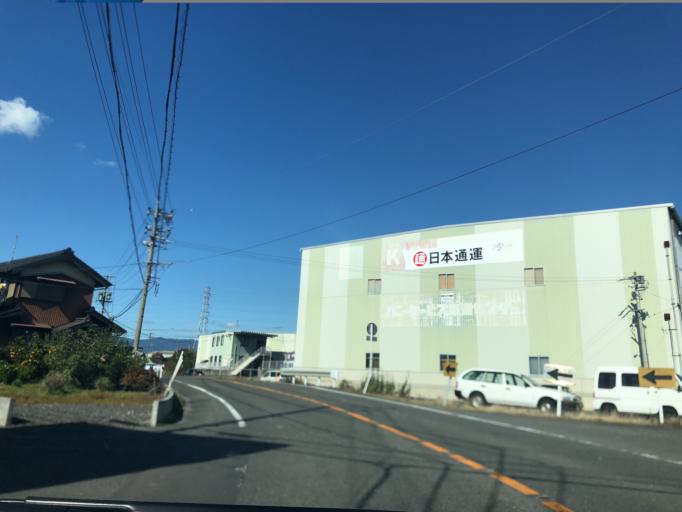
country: JP
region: Gifu
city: Ogaki
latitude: 35.3968
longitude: 136.6656
